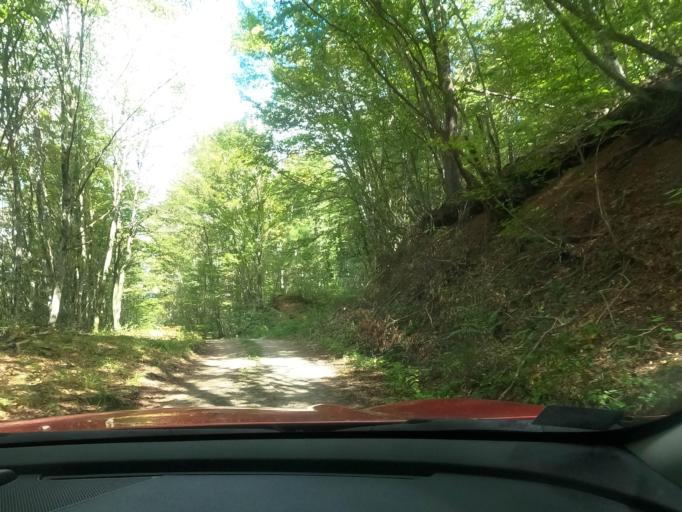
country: BA
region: Federation of Bosnia and Herzegovina
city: Velika Kladusa
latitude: 45.2358
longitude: 15.7758
